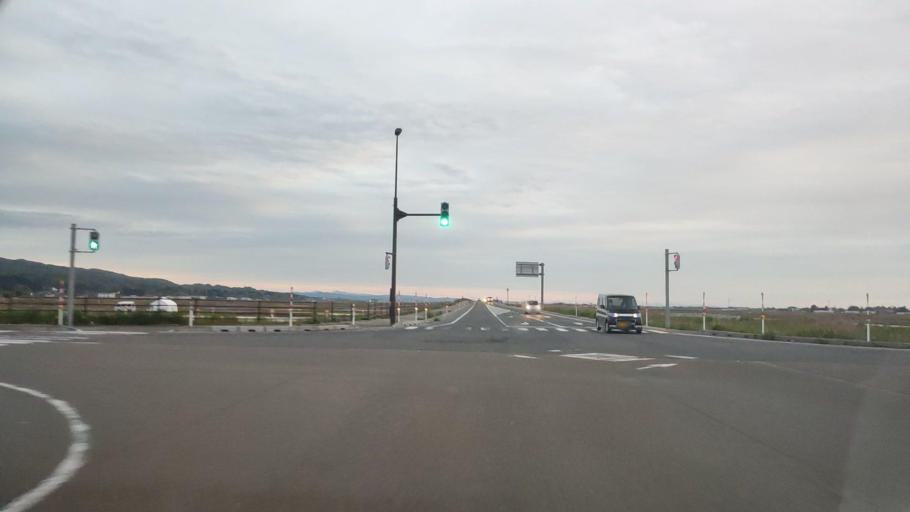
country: JP
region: Niigata
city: Niitsu-honcho
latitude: 37.7512
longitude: 139.0878
